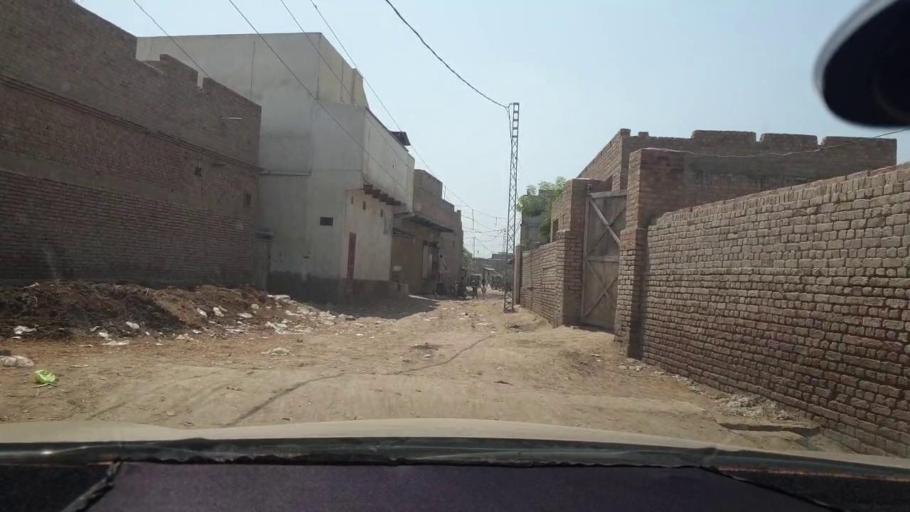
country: PK
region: Sindh
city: Kambar
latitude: 27.6166
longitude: 68.0055
